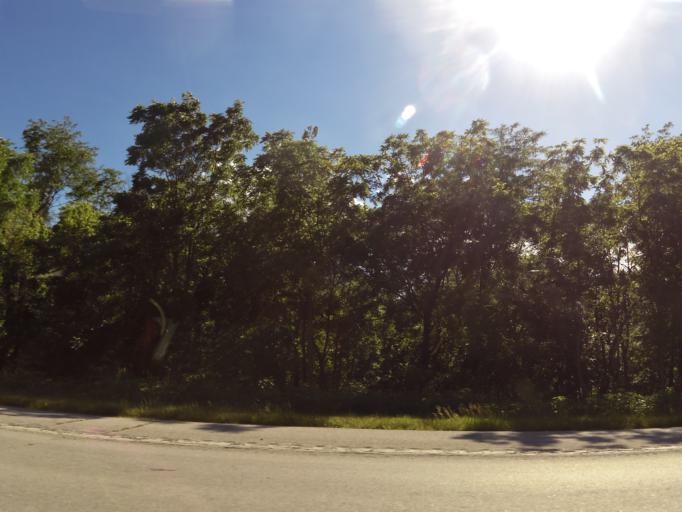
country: US
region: Missouri
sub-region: Lewis County
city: Canton
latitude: 40.1048
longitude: -91.5392
